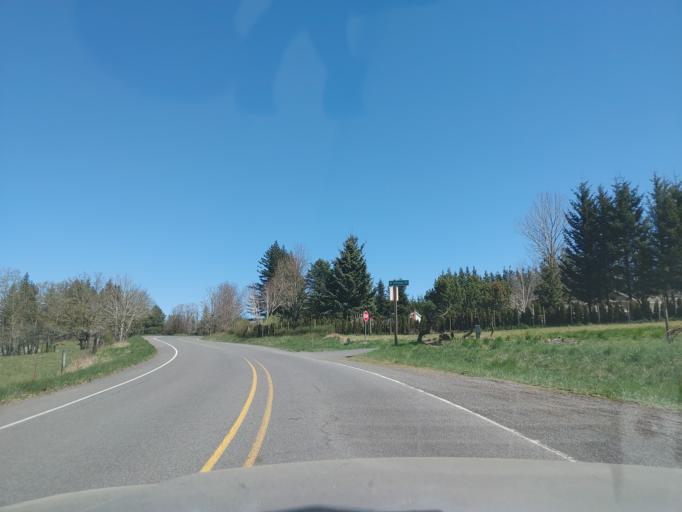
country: US
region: Washington
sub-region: Clark County
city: Washougal
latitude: 45.5298
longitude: -122.2751
